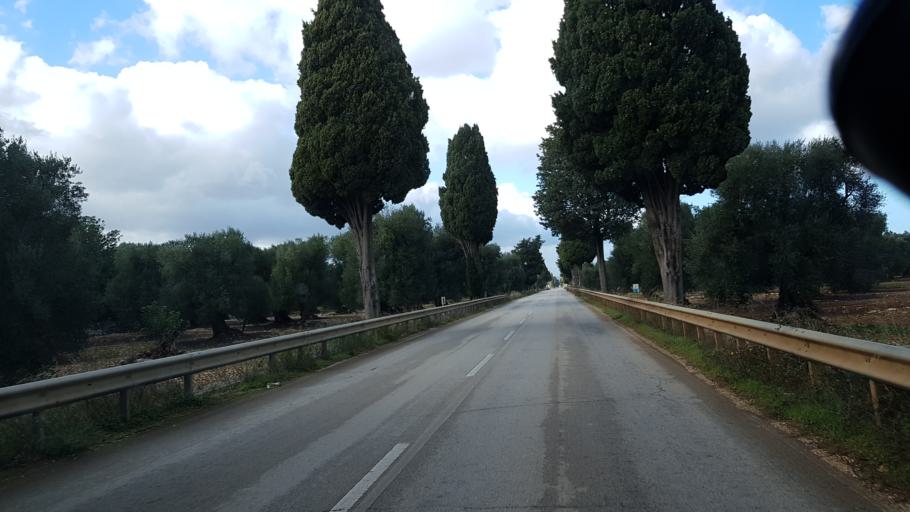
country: IT
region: Apulia
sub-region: Provincia di Brindisi
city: Montalbano
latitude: 40.7703
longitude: 17.5073
